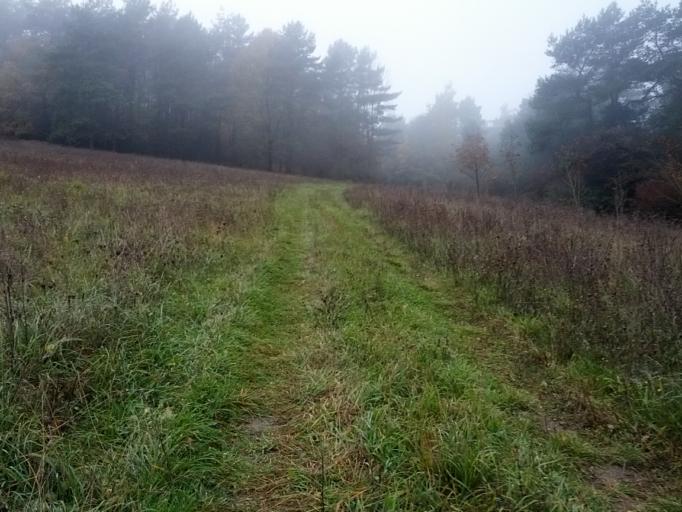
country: DE
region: Thuringia
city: Eisenach
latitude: 50.9833
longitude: 10.3796
